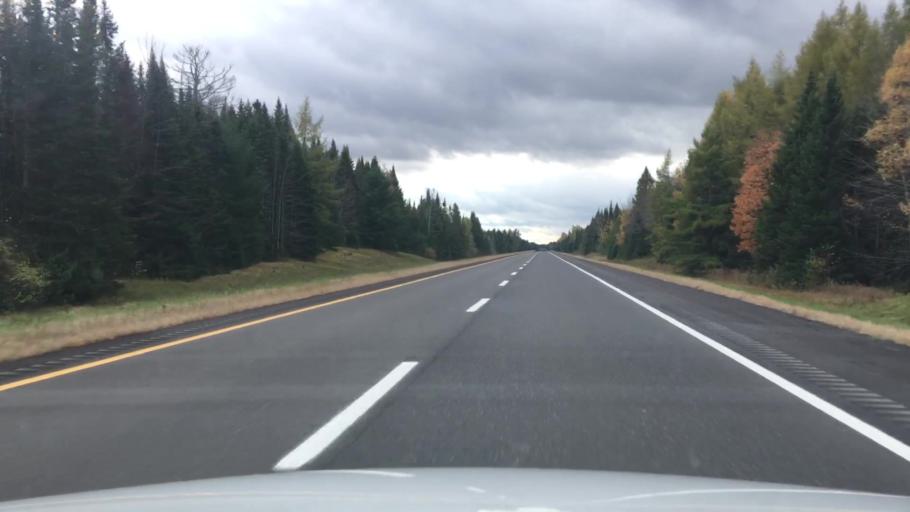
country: US
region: Maine
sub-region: Penobscot County
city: Patten
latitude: 46.0839
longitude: -68.2108
